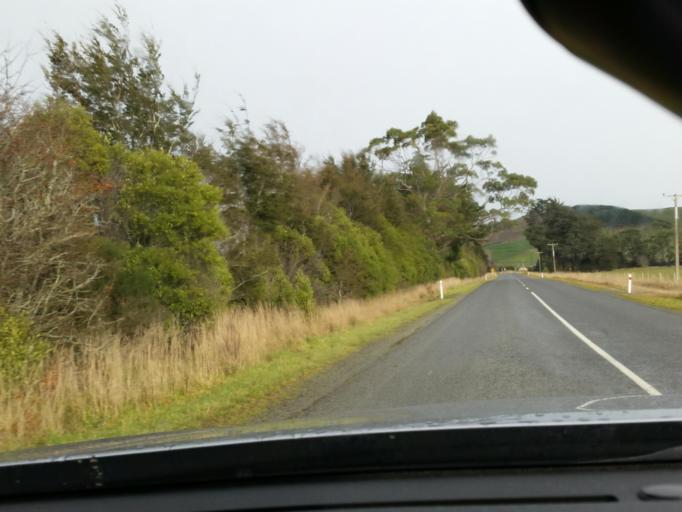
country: NZ
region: Southland
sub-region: Southland District
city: Winton
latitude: -46.0993
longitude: 168.4072
